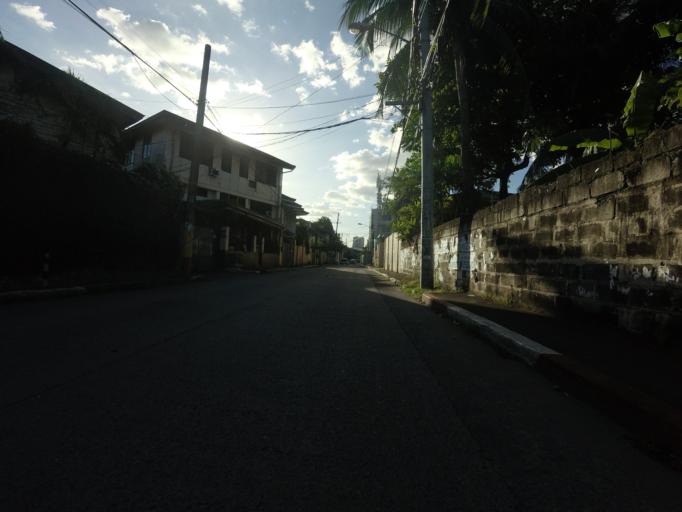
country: PH
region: Metro Manila
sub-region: San Juan
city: San Juan
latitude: 14.5946
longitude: 121.0327
